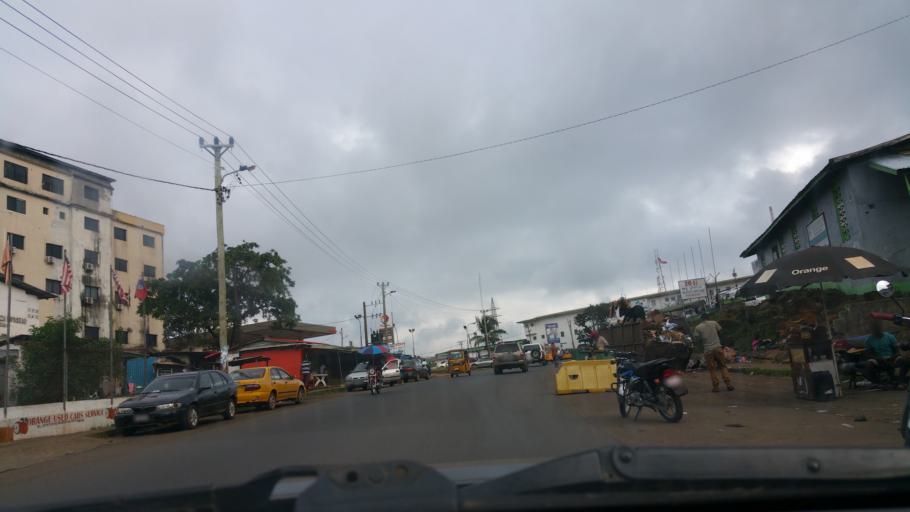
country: LR
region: Montserrado
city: Monrovia
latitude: 6.3050
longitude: -10.7953
